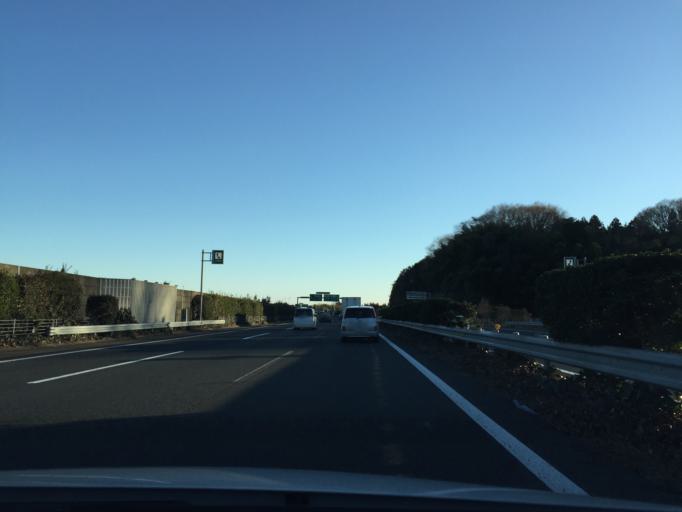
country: JP
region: Tochigi
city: Tochigi
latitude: 36.4320
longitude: 139.7160
